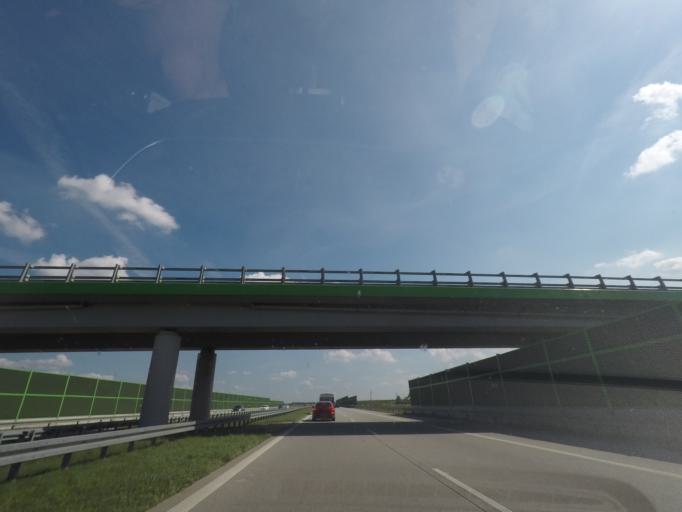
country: PL
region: Lodz Voivodeship
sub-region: Powiat lodzki wschodni
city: Tuszyn
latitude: 51.6017
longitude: 19.5793
